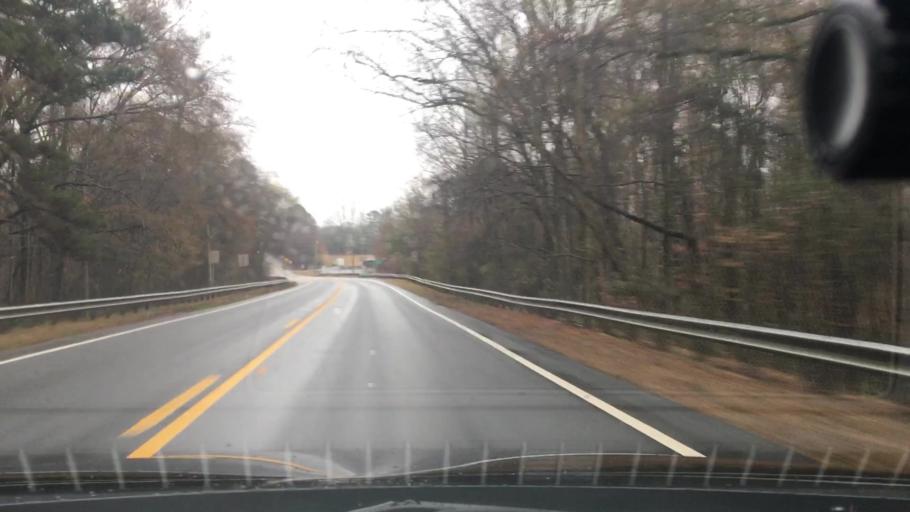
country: US
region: Georgia
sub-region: Coweta County
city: Senoia
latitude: 33.2572
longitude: -84.4993
